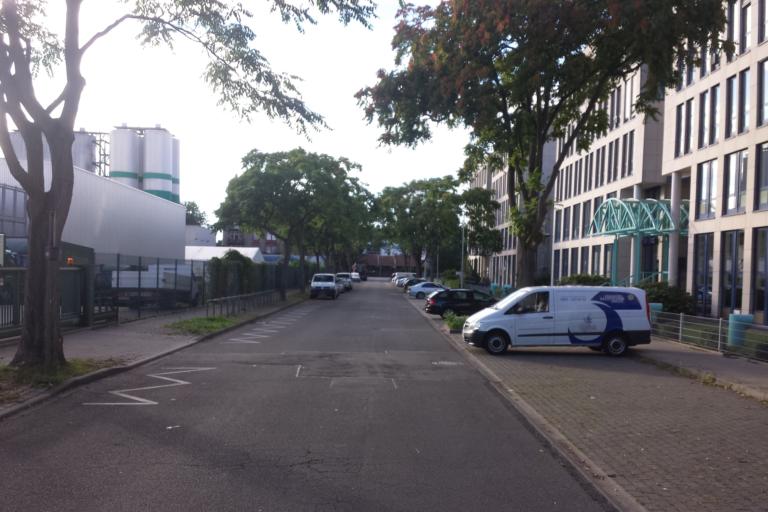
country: DE
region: Baden-Wuerttemberg
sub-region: Karlsruhe Region
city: Mannheim
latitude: 49.4959
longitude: 8.4936
